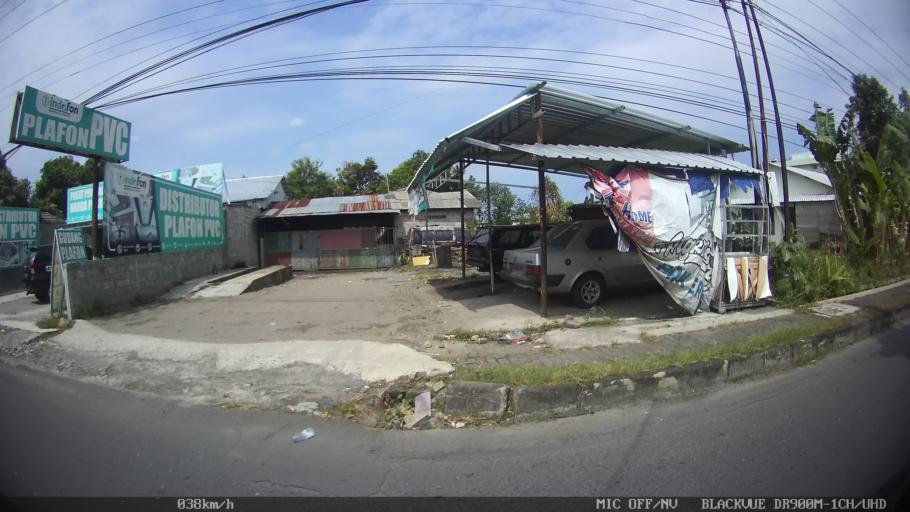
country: ID
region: Daerah Istimewa Yogyakarta
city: Depok
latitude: -7.7653
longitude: 110.4315
